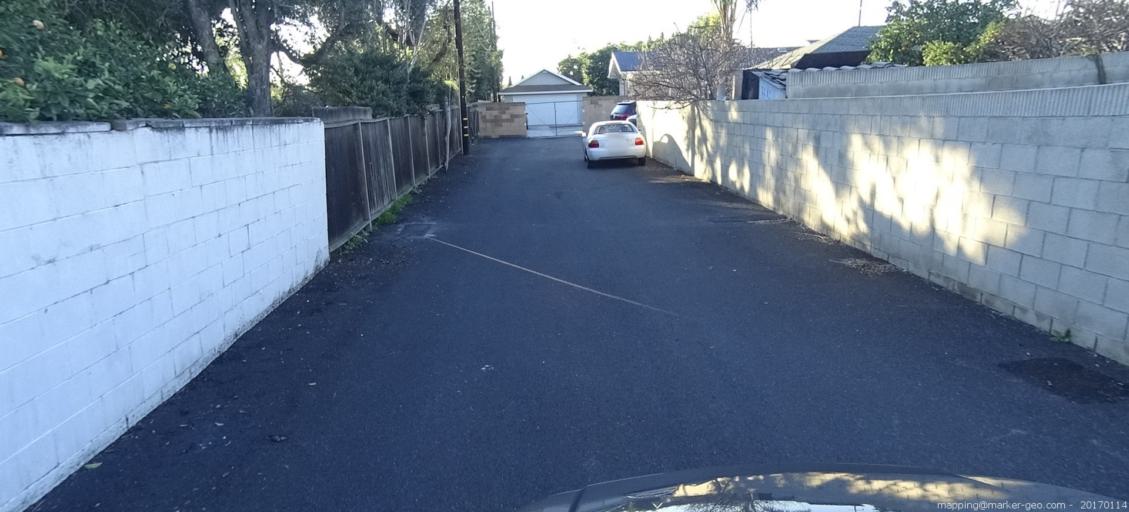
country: US
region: California
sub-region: Orange County
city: Tustin
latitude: 33.7595
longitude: -117.8148
